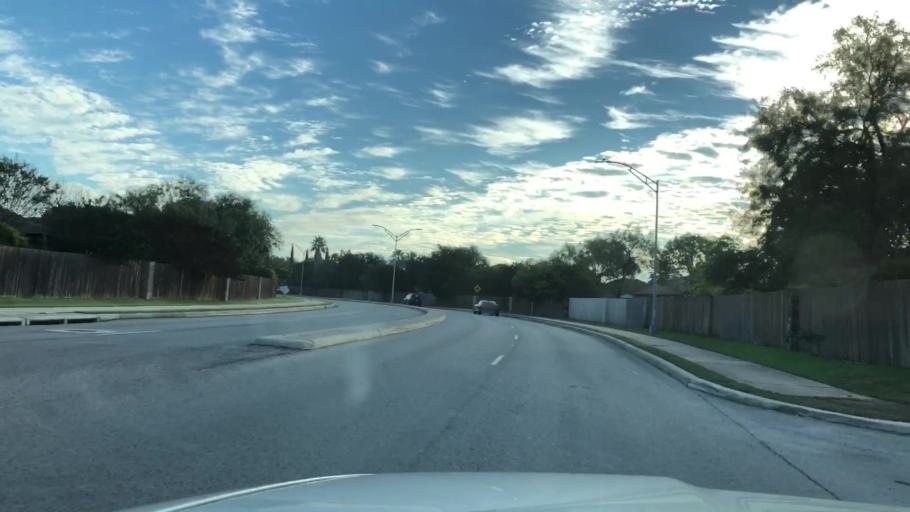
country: US
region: Texas
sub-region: Bexar County
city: Leon Valley
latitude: 29.5415
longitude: -98.6306
